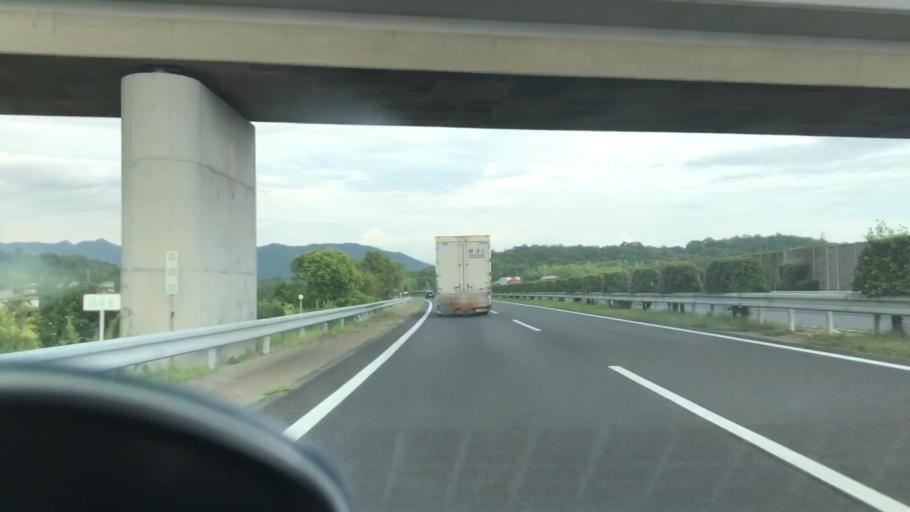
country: JP
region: Hyogo
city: Yashiro
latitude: 34.9302
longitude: 134.9119
